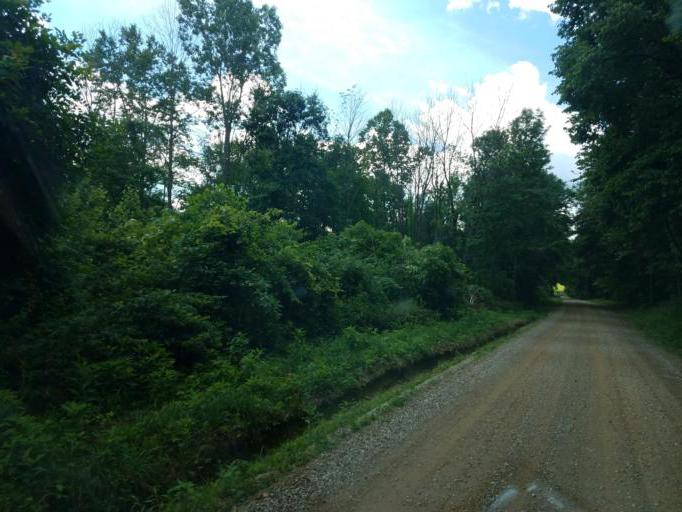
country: US
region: Ohio
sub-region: Knox County
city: Danville
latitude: 40.4395
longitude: -82.2918
